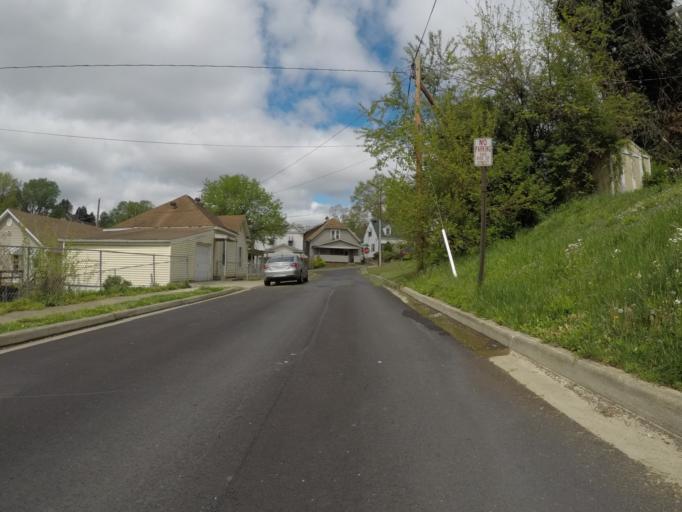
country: US
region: West Virginia
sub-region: Cabell County
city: Huntington
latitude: 38.4096
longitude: -82.4059
